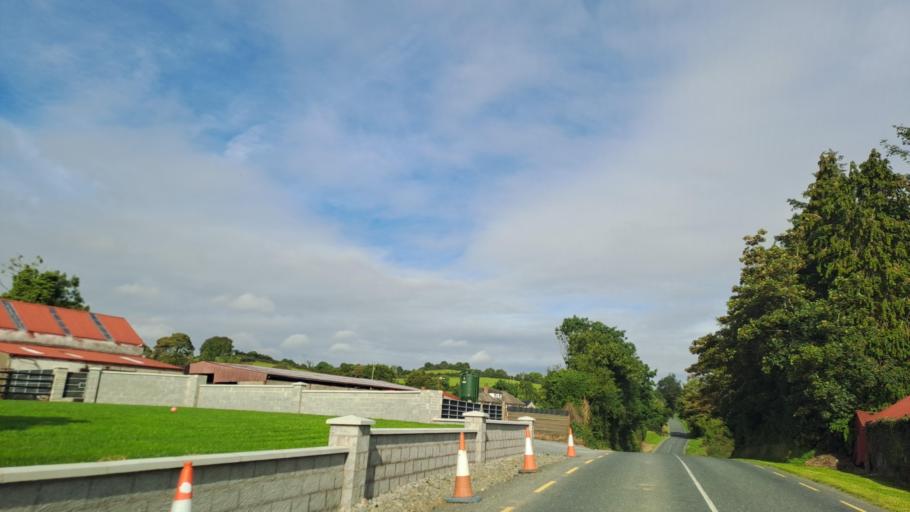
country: IE
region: Ulster
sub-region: An Cabhan
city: Kingscourt
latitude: 53.9507
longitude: -6.8402
